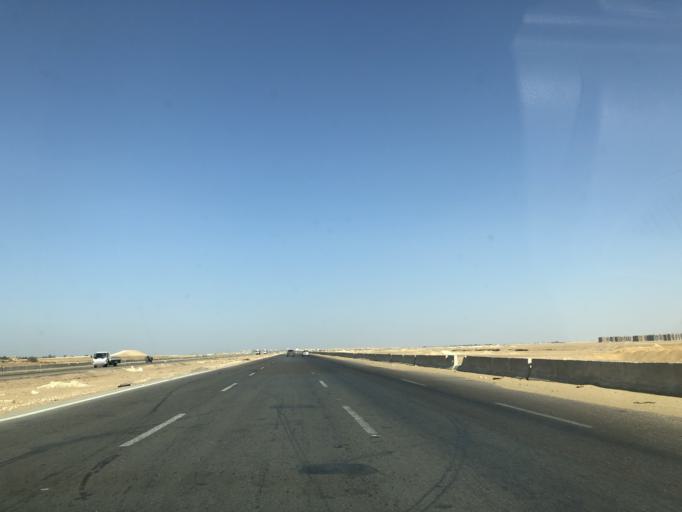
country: EG
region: Muhafazat al Minufiyah
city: Ashmun
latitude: 30.0677
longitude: 30.8787
